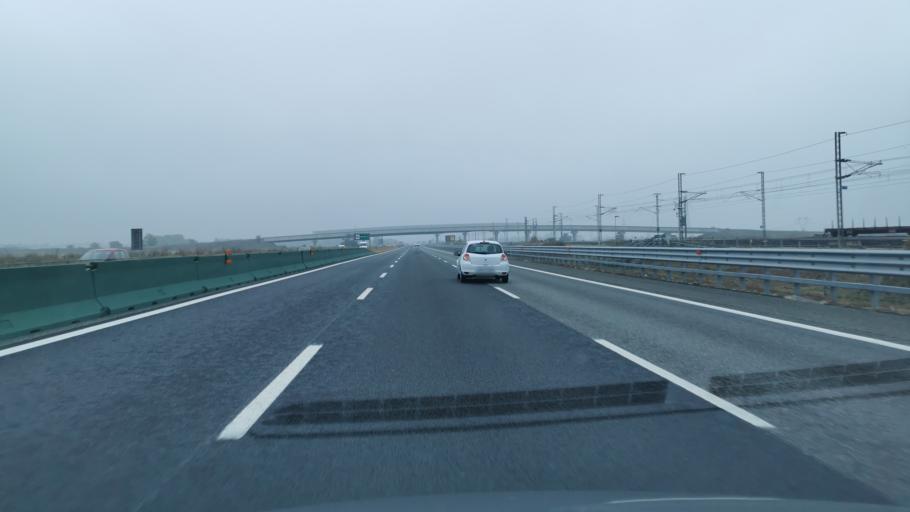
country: IT
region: Piedmont
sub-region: Provincia di Vercelli
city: Alice Castello
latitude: 45.3511
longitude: 8.1052
